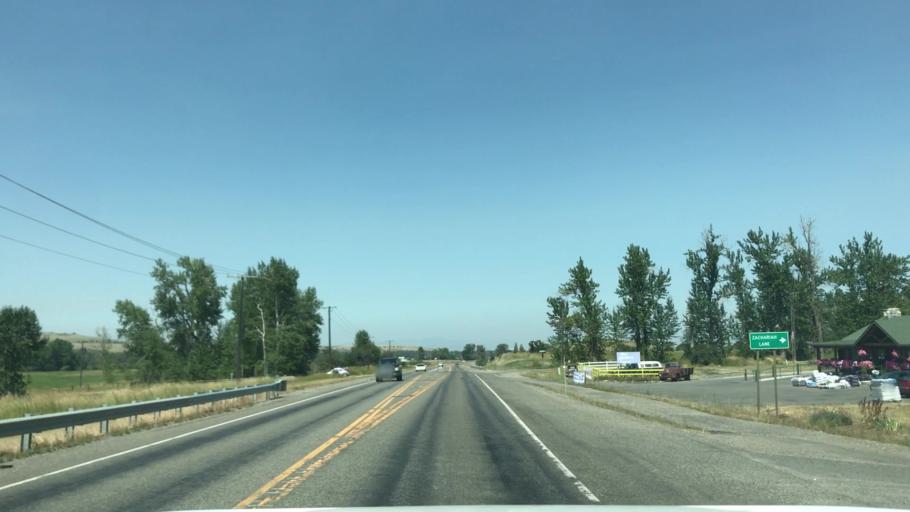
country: US
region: Montana
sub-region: Gallatin County
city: Four Corners
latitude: 45.6117
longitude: -111.1961
